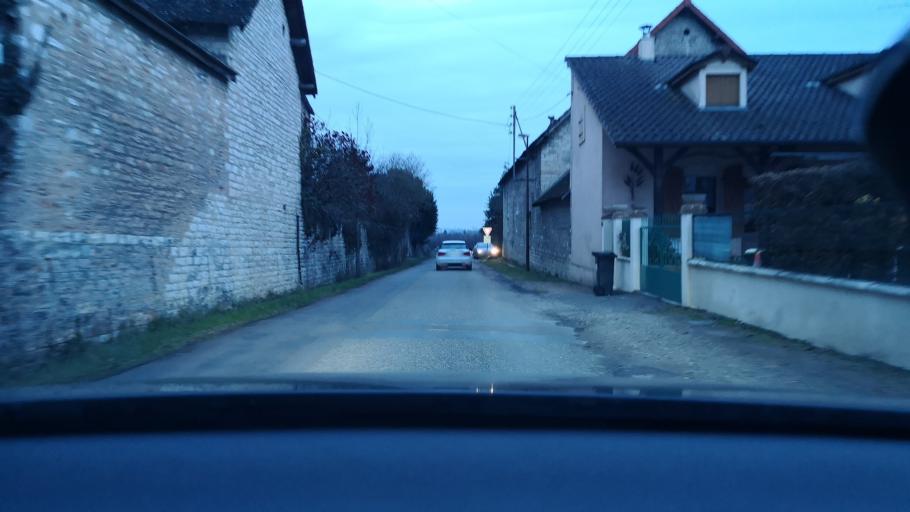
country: FR
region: Bourgogne
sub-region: Departement de Saone-et-Loire
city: Saint-Remy
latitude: 46.7696
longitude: 4.8170
